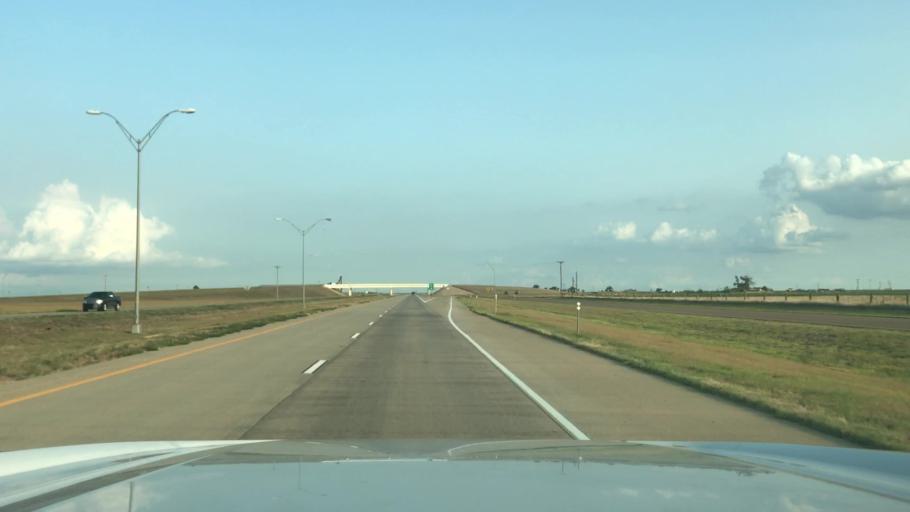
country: US
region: Texas
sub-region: Hale County
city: Seth Ward
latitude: 34.3492
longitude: -101.7507
